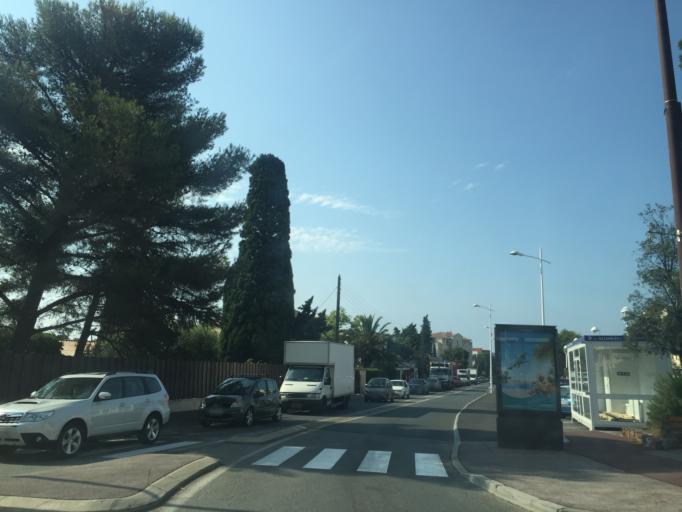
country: FR
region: Provence-Alpes-Cote d'Azur
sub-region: Departement du Var
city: Frejus
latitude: 43.3844
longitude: 6.7222
